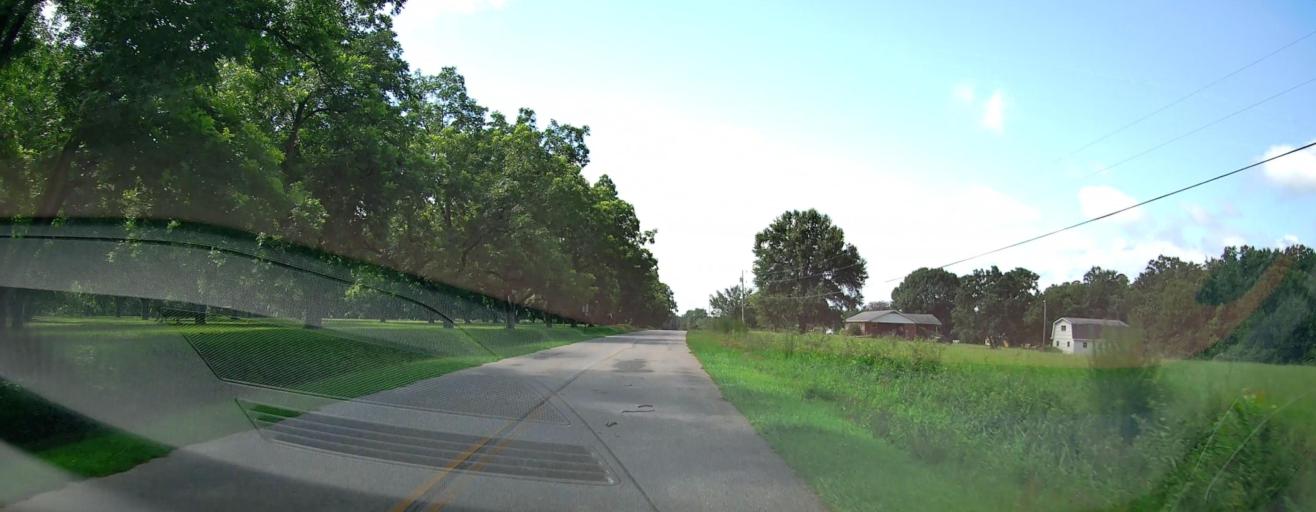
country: US
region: Georgia
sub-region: Peach County
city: Byron
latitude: 32.6580
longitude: -83.7813
